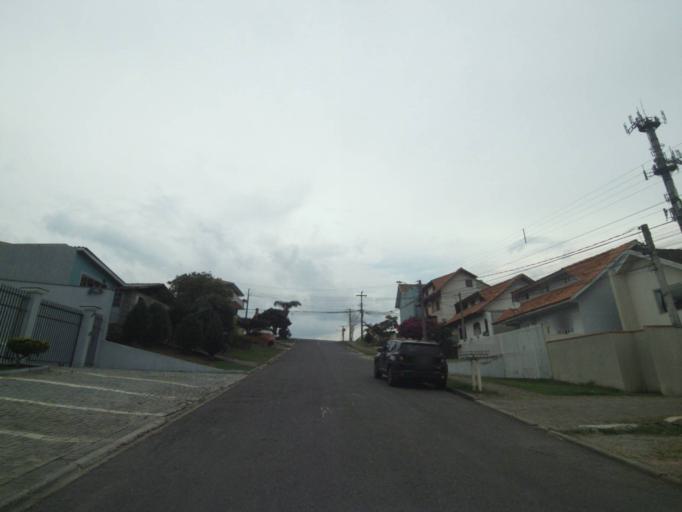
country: BR
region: Parana
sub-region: Pinhais
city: Pinhais
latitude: -25.3996
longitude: -49.2033
